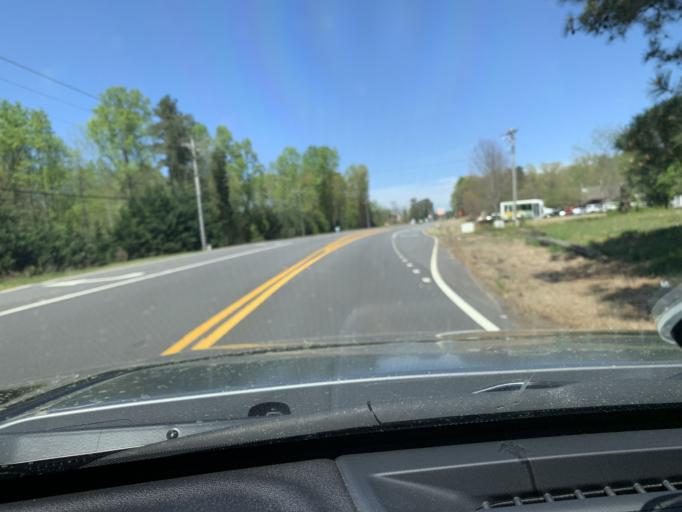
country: US
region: Georgia
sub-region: Forsyth County
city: Cumming
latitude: 34.2322
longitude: -84.2290
